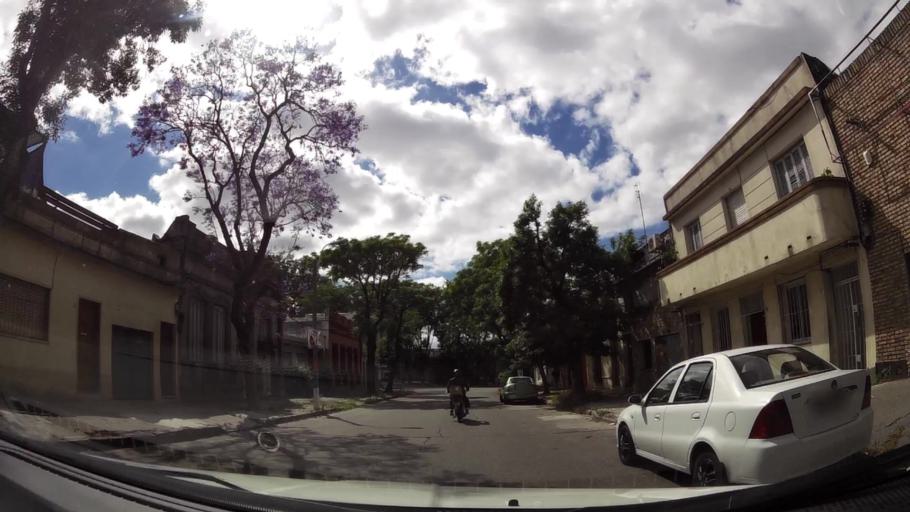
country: UY
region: Montevideo
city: Montevideo
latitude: -34.8795
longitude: -56.1768
